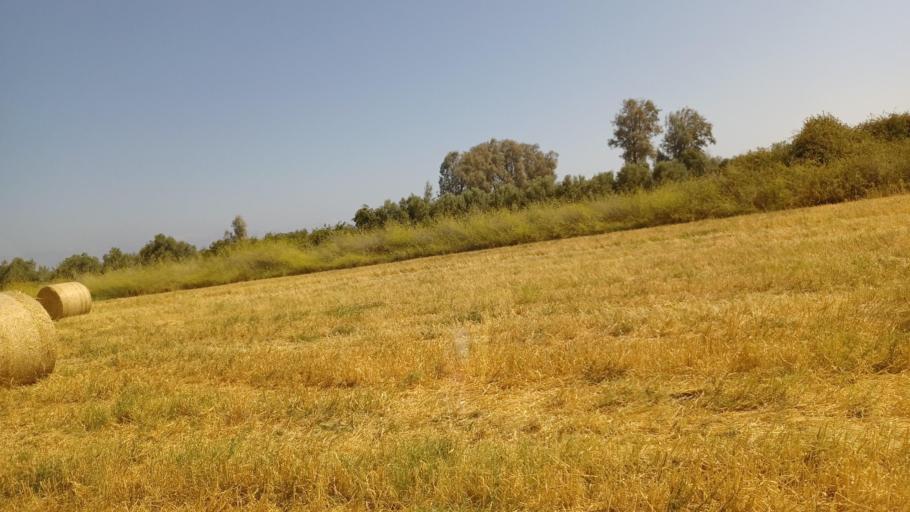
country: CY
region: Pafos
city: Polis
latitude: 35.0431
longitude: 32.4242
